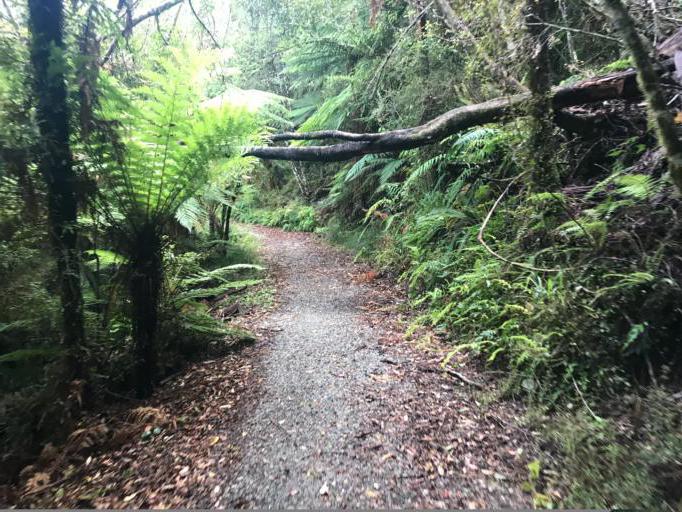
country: NZ
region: West Coast
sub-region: Westland District
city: Hokitika
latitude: -42.7649
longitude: 171.2483
